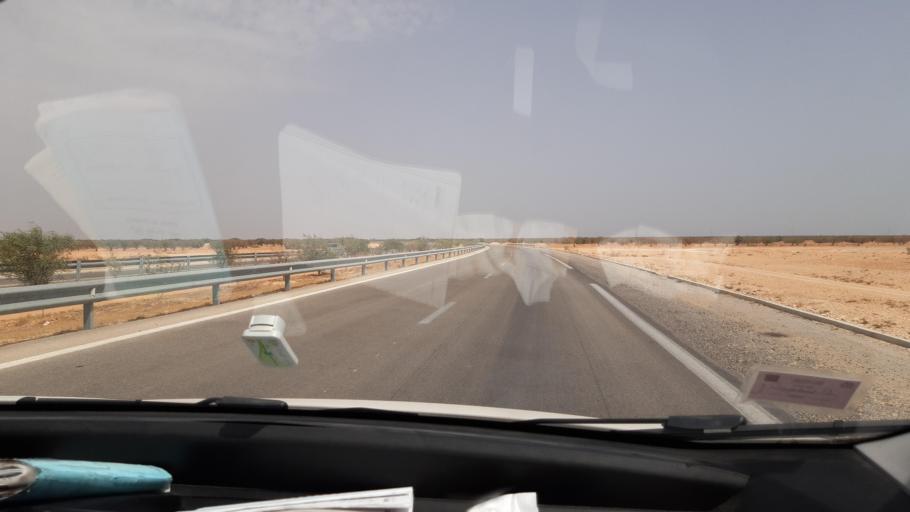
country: TN
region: Safaqis
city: Bi'r `Ali Bin Khalifah
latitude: 34.5667
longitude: 10.3691
